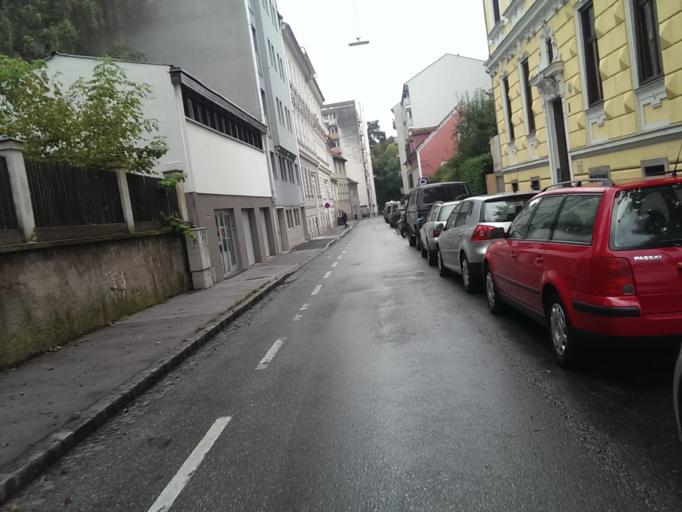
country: AT
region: Styria
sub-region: Graz Stadt
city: Graz
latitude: 47.0722
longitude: 15.4547
